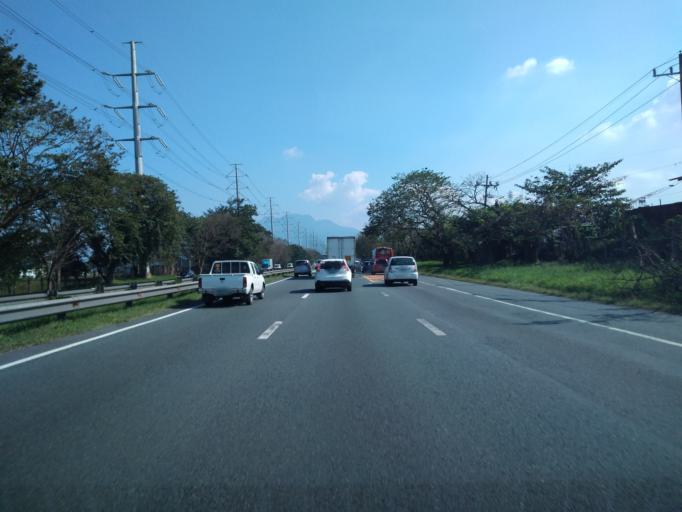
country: PH
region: Calabarzon
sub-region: Province of Laguna
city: Prinza
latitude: 14.2265
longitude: 121.1206
